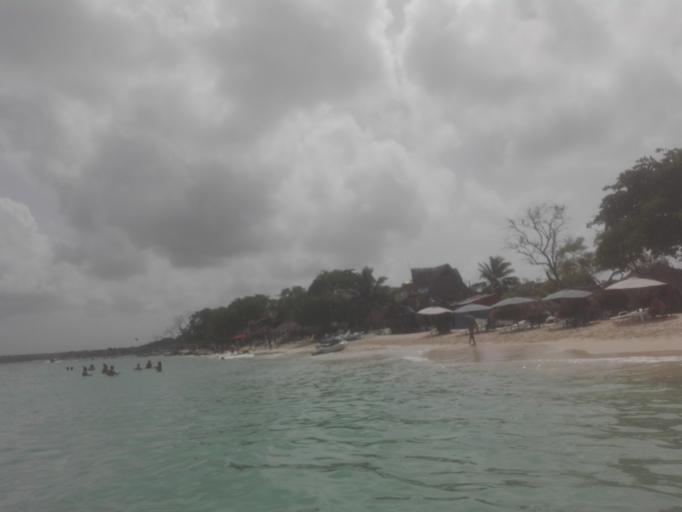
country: CO
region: Bolivar
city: Turbana
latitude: 10.2203
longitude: -75.6110
